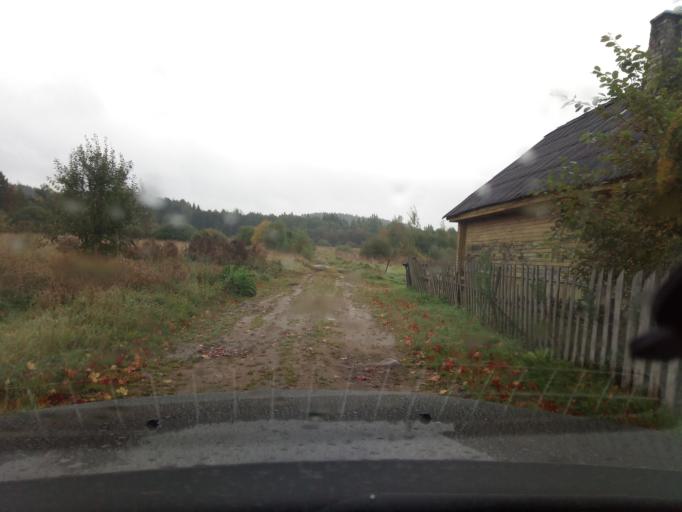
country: LT
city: Skaidiskes
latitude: 54.5985
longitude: 25.5844
